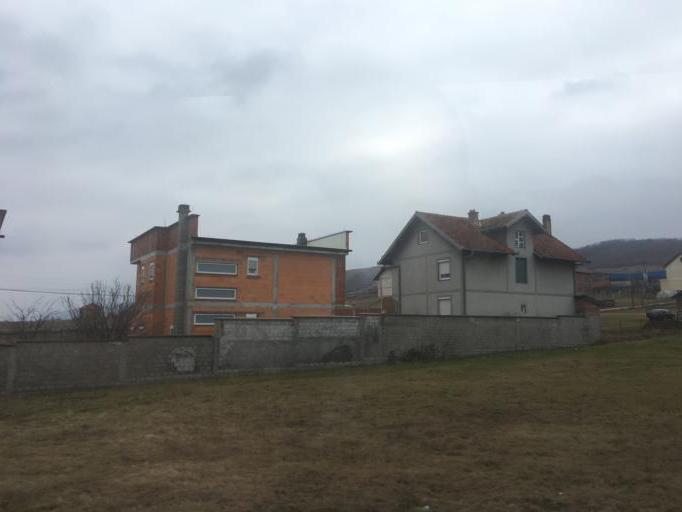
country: XK
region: Pristina
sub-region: Komuna e Drenasit
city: Glogovac
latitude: 42.5755
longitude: 20.8727
